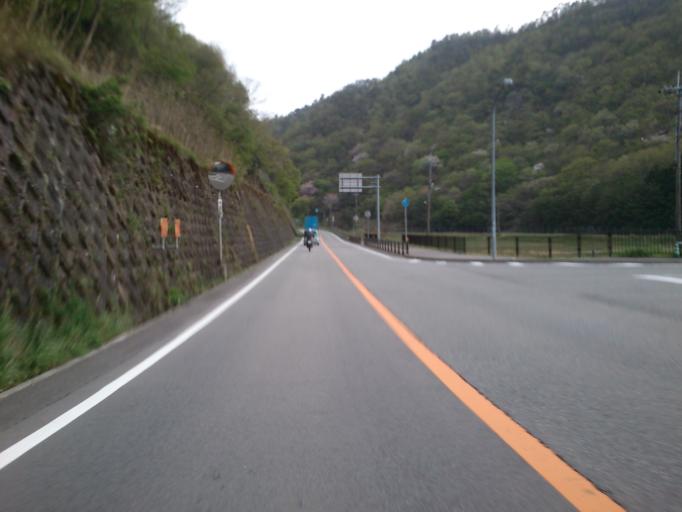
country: JP
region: Hyogo
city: Sasayama
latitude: 35.1368
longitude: 135.3325
